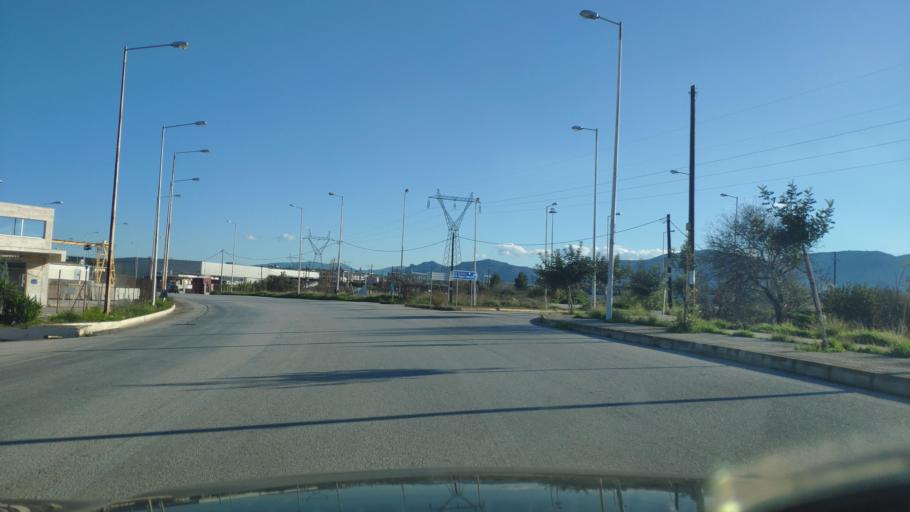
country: GR
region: Peloponnese
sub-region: Nomos Korinthias
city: Korinthos
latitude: 37.9244
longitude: 22.9316
